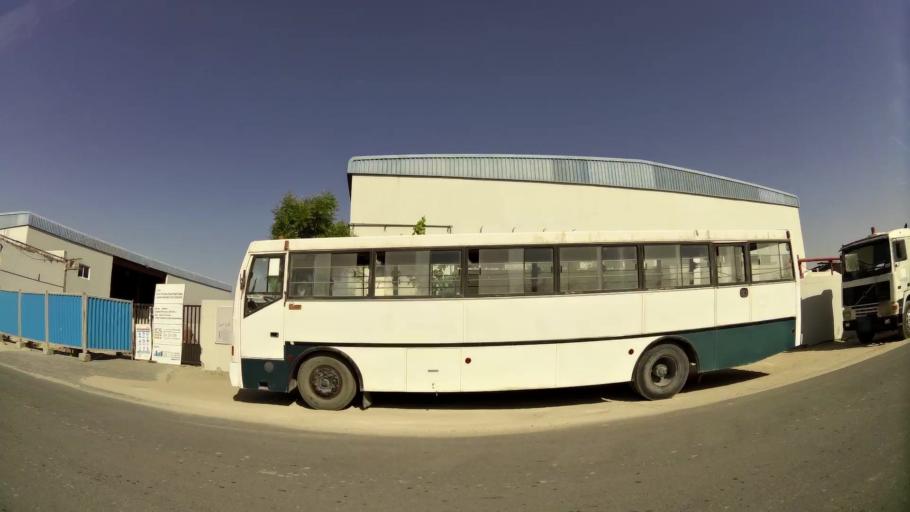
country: AE
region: Dubai
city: Dubai
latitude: 24.9902
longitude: 55.1070
